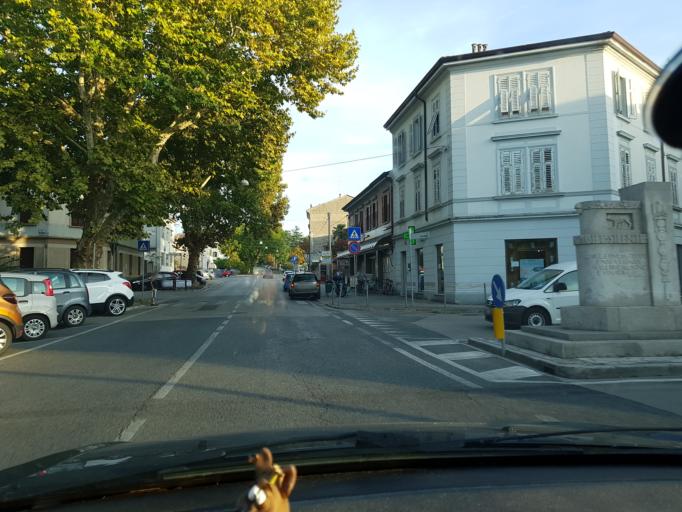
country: IT
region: Friuli Venezia Giulia
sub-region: Provincia di Gorizia
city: Gorizia
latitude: 45.9560
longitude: 13.6147
